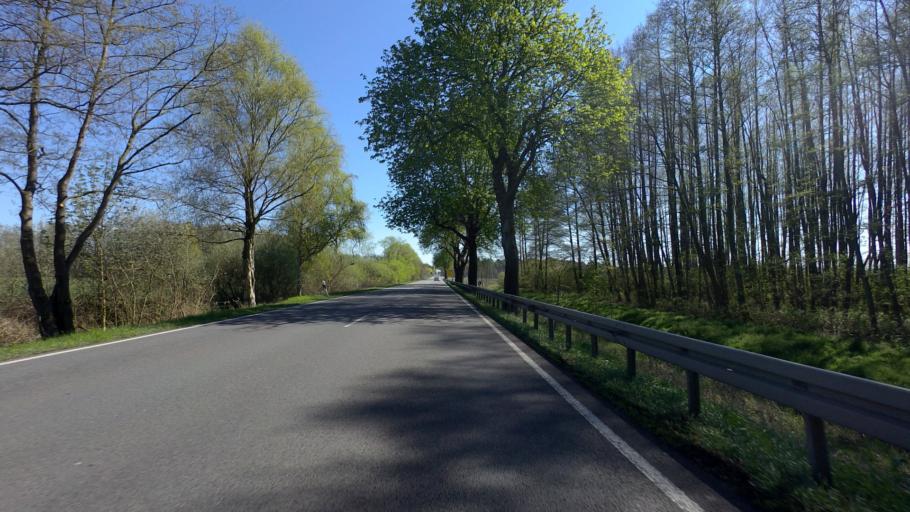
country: DE
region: Saxony-Anhalt
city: Klotze
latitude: 52.6903
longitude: 11.2637
